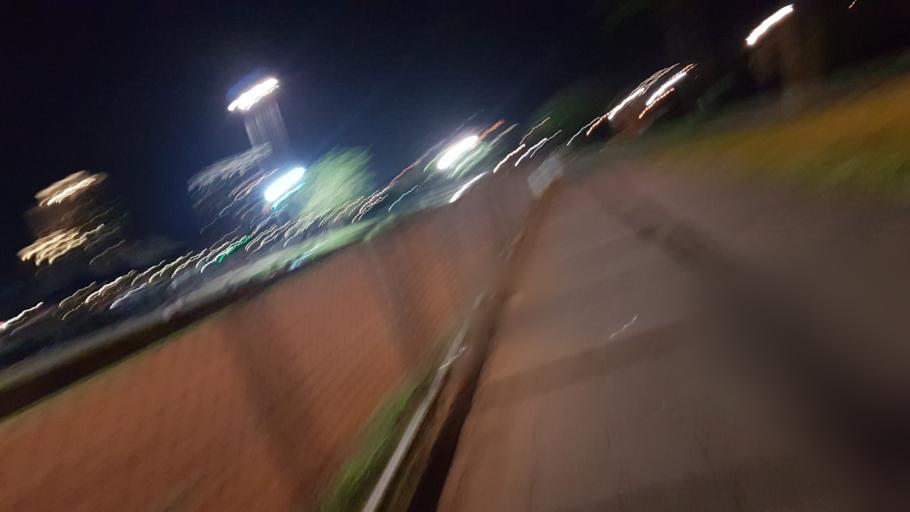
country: TW
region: Taipei
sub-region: Taipei
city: Banqiao
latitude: 24.9768
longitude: 121.5197
